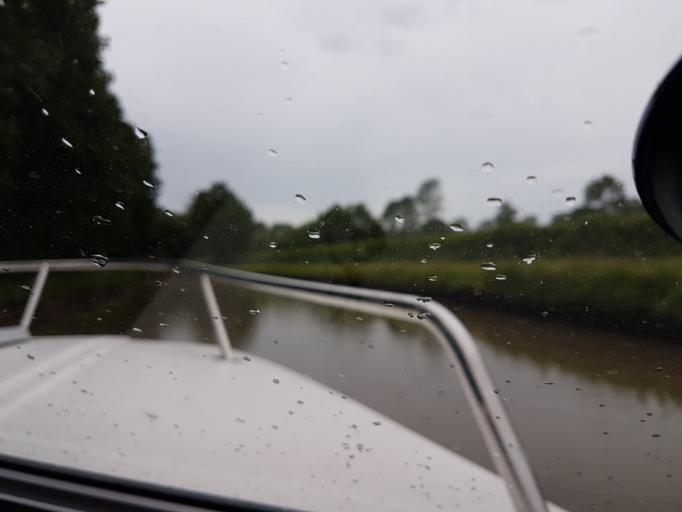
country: FR
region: Bourgogne
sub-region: Departement de la Nievre
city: Clamecy
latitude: 47.3669
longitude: 3.6115
